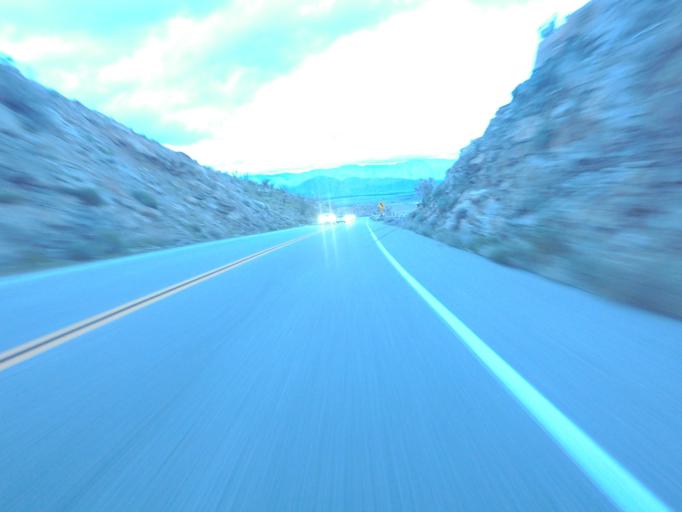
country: US
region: California
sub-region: San Diego County
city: Borrego Springs
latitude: 33.2306
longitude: -116.4100
